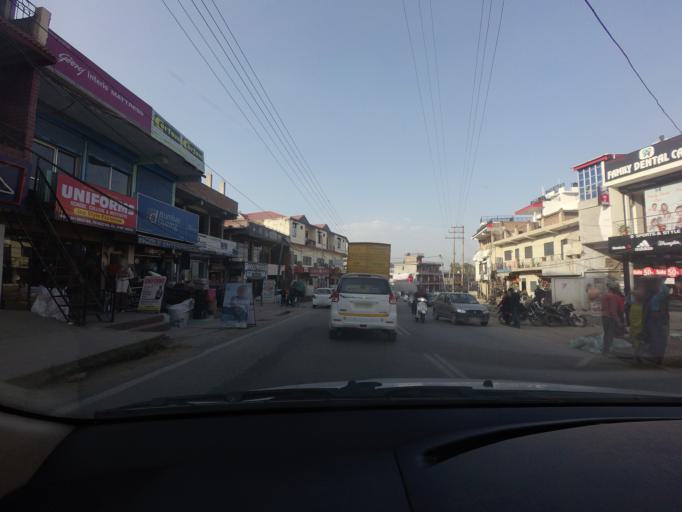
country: IN
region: Himachal Pradesh
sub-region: Mandi
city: Sundarnagar
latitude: 31.5317
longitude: 76.8881
